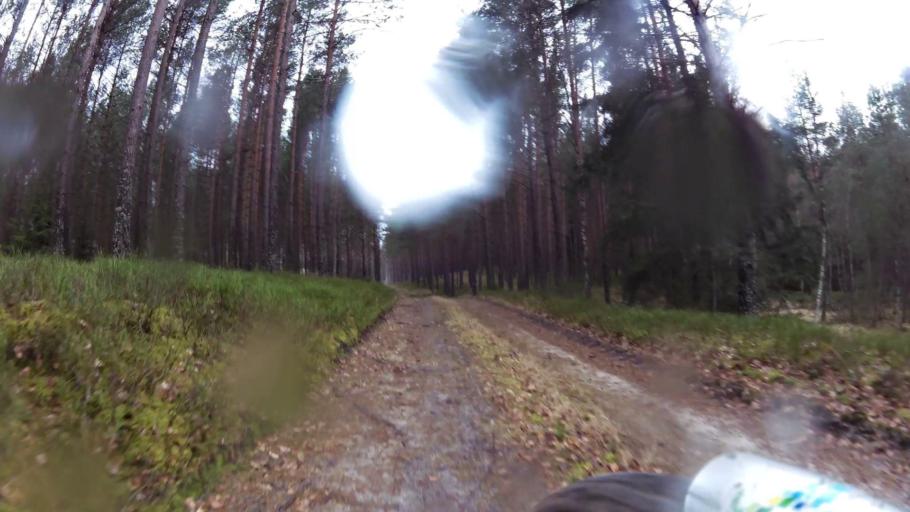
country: PL
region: Pomeranian Voivodeship
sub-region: Powiat bytowski
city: Trzebielino
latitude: 54.0778
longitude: 17.1012
